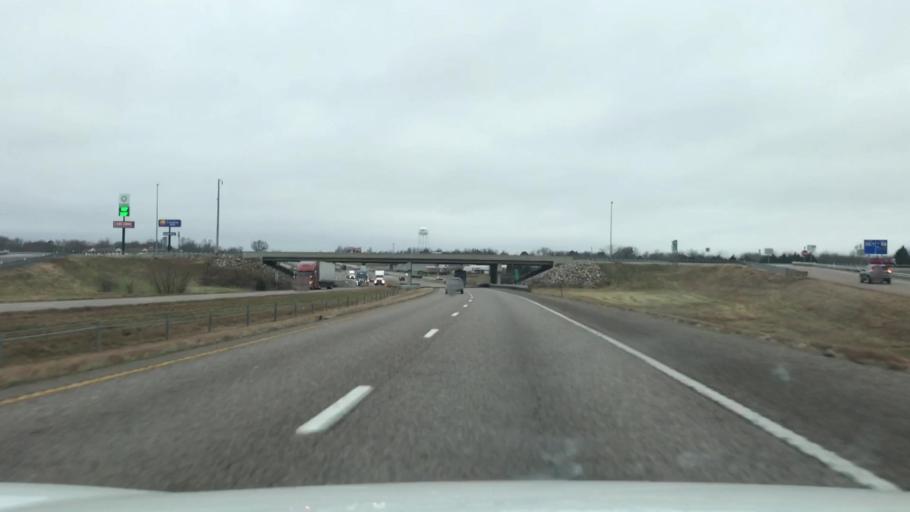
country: US
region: Missouri
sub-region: Franklin County
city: Sullivan
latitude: 38.2131
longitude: -91.1710
